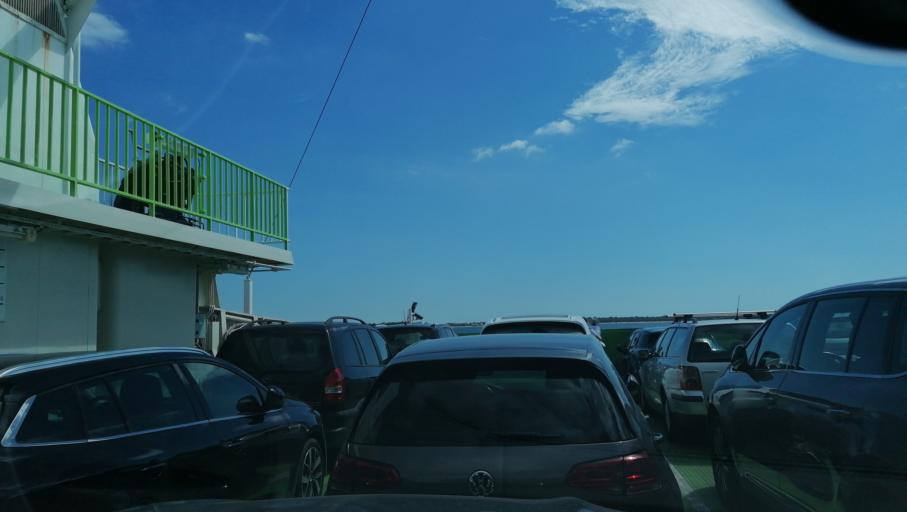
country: PT
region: Setubal
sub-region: Setubal
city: Setubal
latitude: 38.5083
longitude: -8.8848
